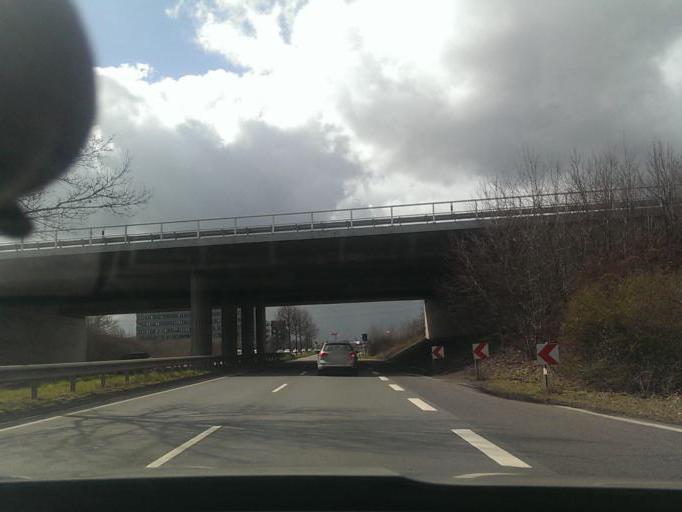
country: DE
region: Lower Saxony
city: Wolfsburg
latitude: 52.4231
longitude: 10.7388
